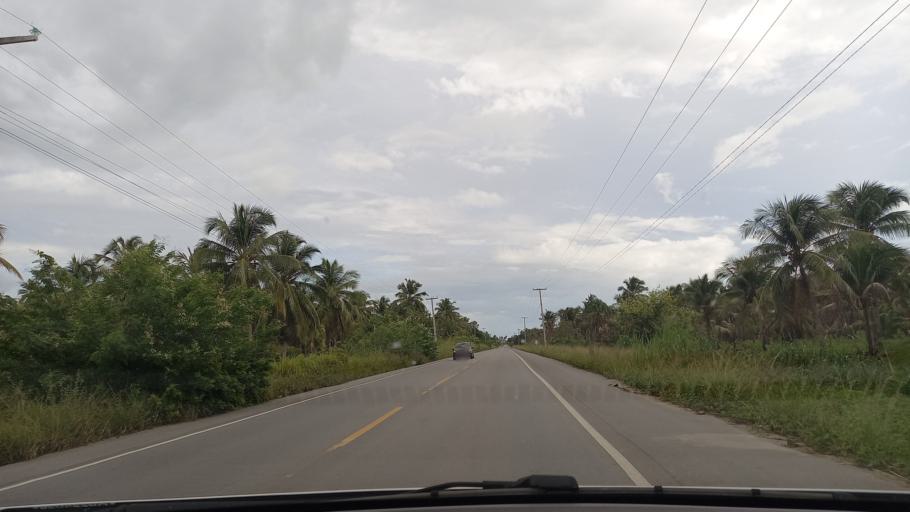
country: BR
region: Alagoas
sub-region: Maragogi
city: Maragogi
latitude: -8.9626
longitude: -35.1806
